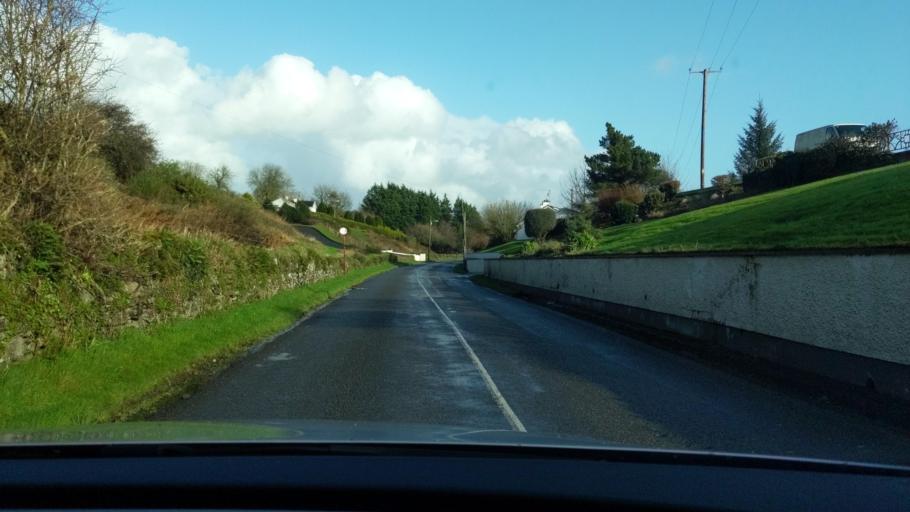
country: IE
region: Munster
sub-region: County Cork
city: Cork
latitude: 51.9266
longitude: -8.5056
